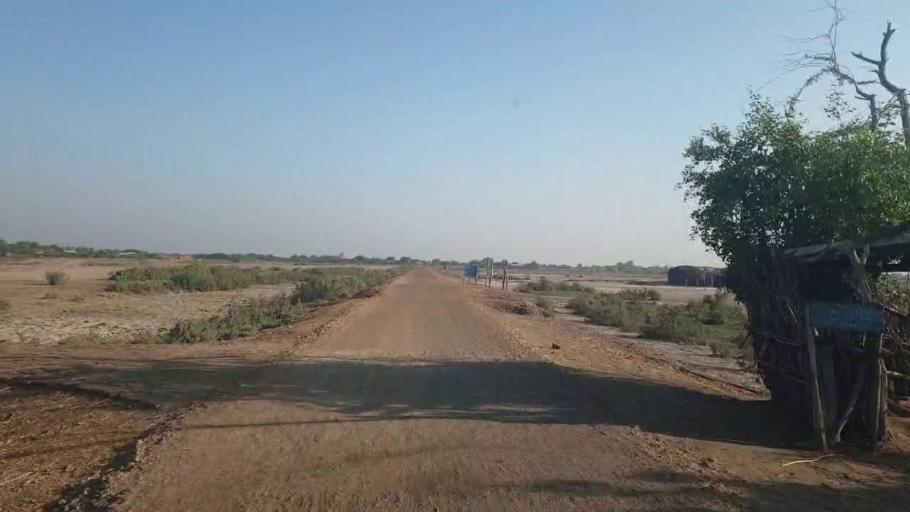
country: PK
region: Sindh
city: Badin
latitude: 24.7258
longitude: 68.8645
